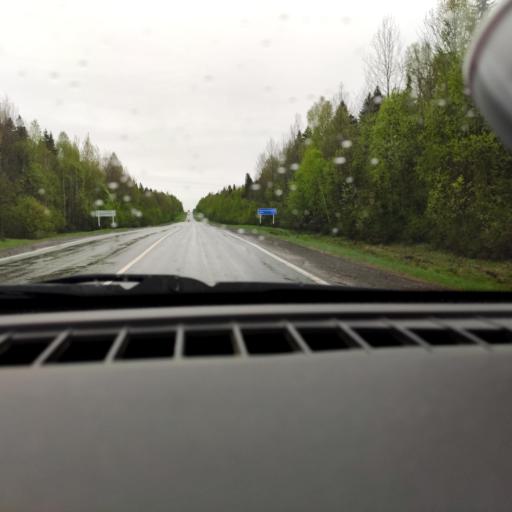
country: RU
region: Perm
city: Perm
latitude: 58.1600
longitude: 56.2465
